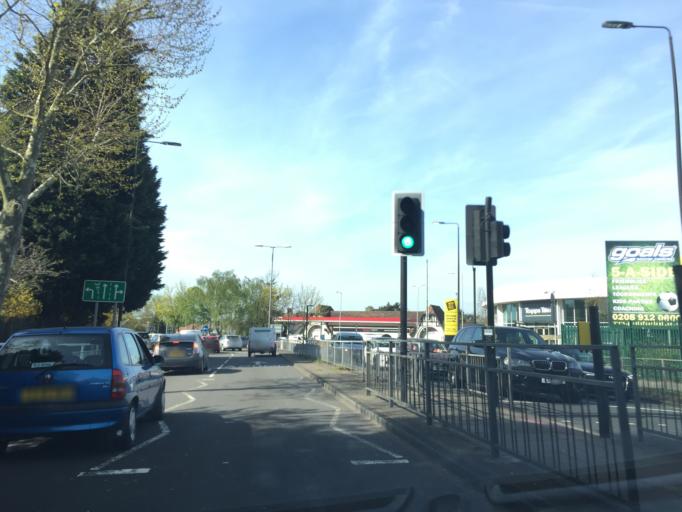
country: GB
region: England
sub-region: Greater London
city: Blackheath
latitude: 51.4493
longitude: 0.0297
